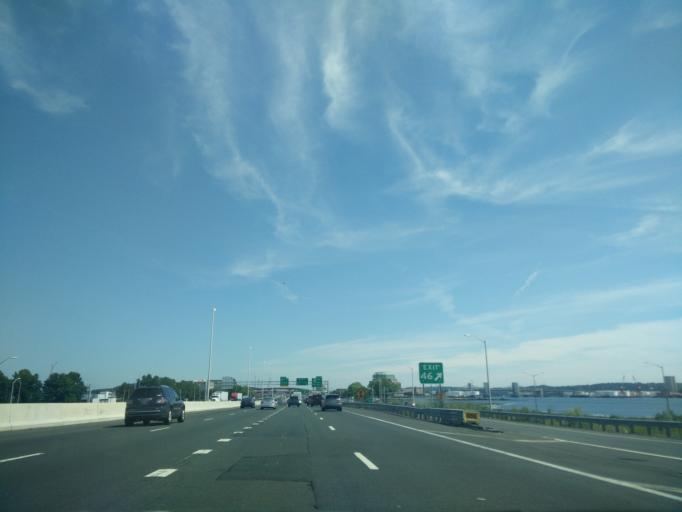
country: US
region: Connecticut
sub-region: New Haven County
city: New Haven
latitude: 41.2876
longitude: -72.9244
